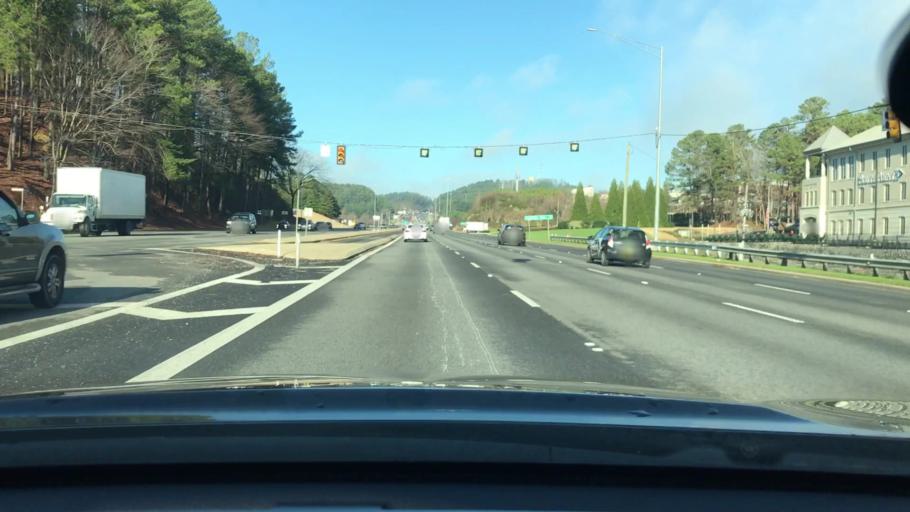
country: US
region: Alabama
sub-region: Jefferson County
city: Cahaba Heights
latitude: 33.4373
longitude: -86.7218
